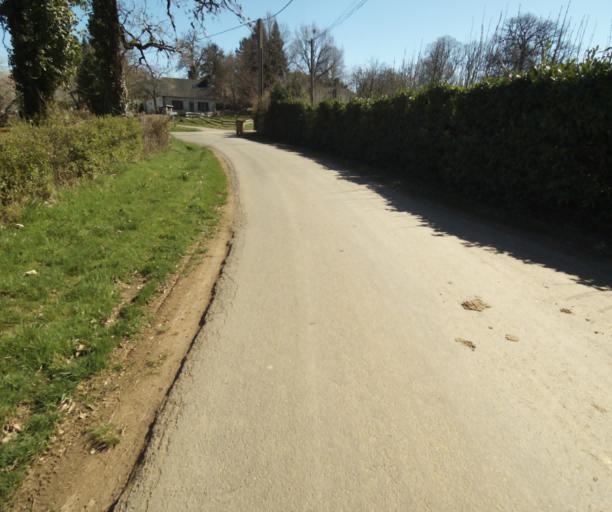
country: FR
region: Limousin
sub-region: Departement de la Correze
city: Seilhac
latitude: 45.3823
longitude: 1.6866
